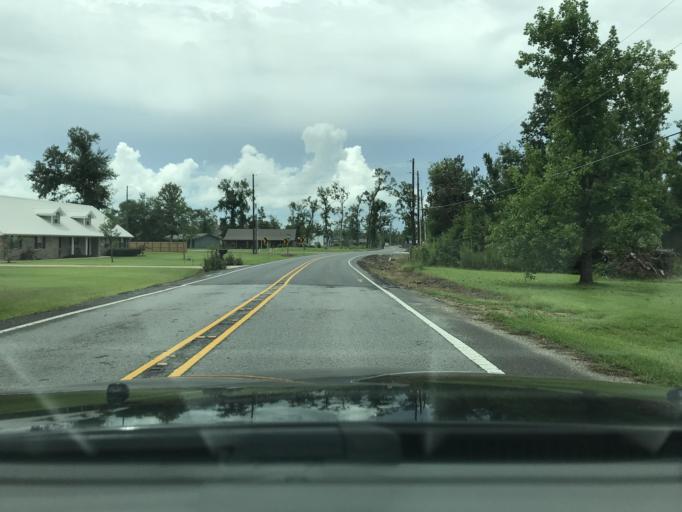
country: US
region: Louisiana
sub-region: Calcasieu Parish
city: Moss Bluff
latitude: 30.3074
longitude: -93.1812
